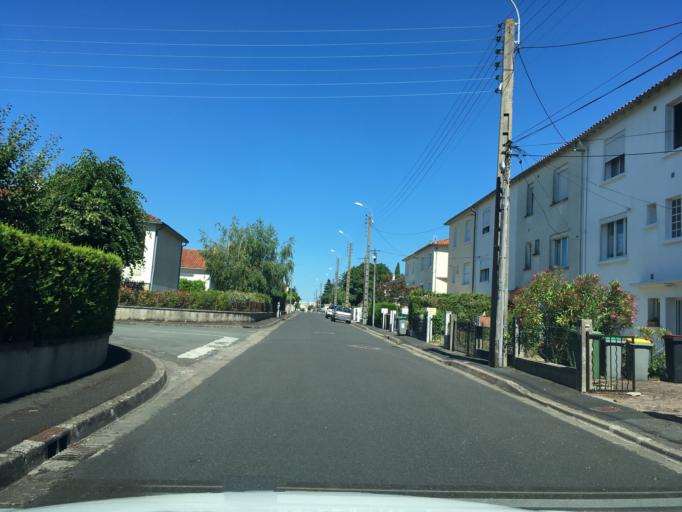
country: FR
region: Poitou-Charentes
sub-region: Departement des Deux-Sevres
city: Niort
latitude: 46.3278
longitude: -0.4359
